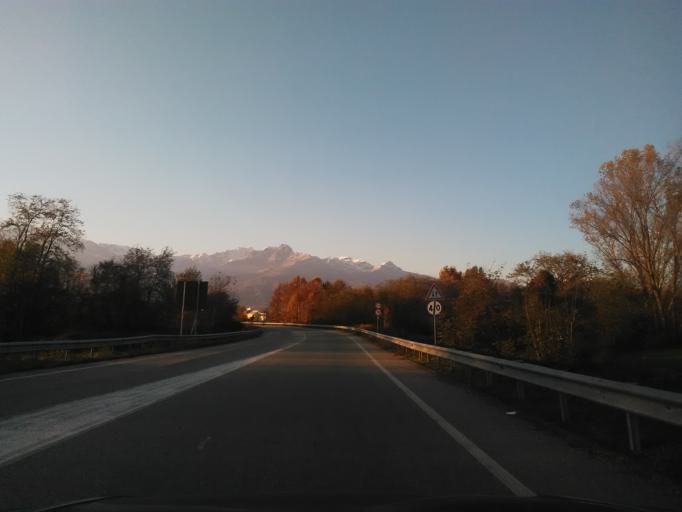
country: IT
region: Piedmont
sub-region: Provincia di Biella
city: Ponderano
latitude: 45.5260
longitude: 8.0477
